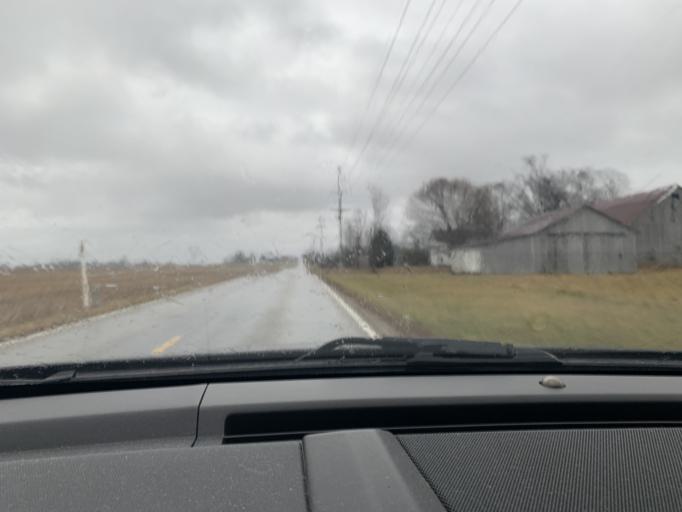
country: US
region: Ohio
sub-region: Ross County
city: Kingston
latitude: 39.4742
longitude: -82.8658
